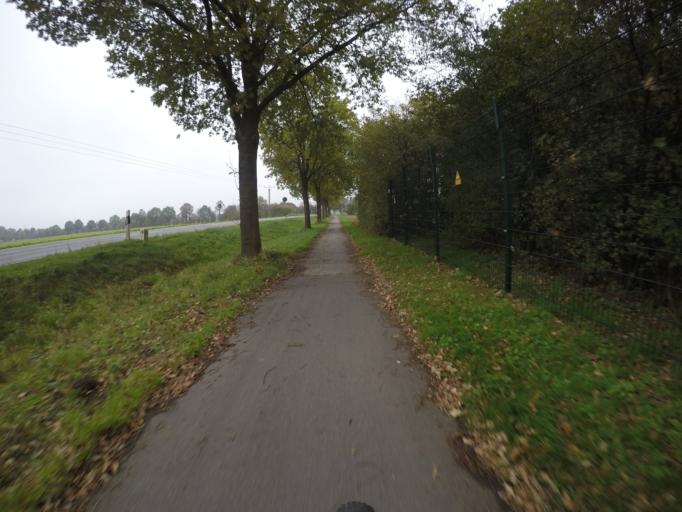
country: DE
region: North Rhine-Westphalia
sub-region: Regierungsbezirk Dusseldorf
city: Bocholt
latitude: 51.8166
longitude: 6.5664
